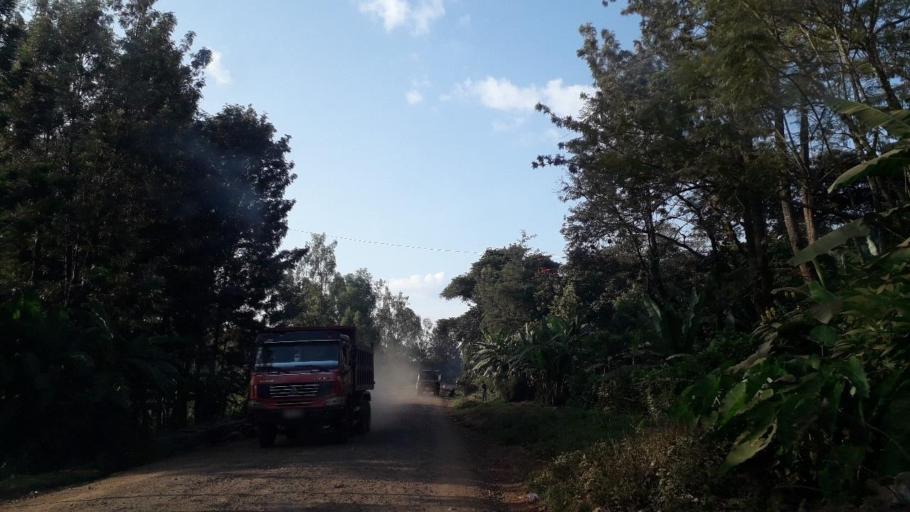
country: ET
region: Oromiya
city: Jima
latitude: 7.5817
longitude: 36.8585
